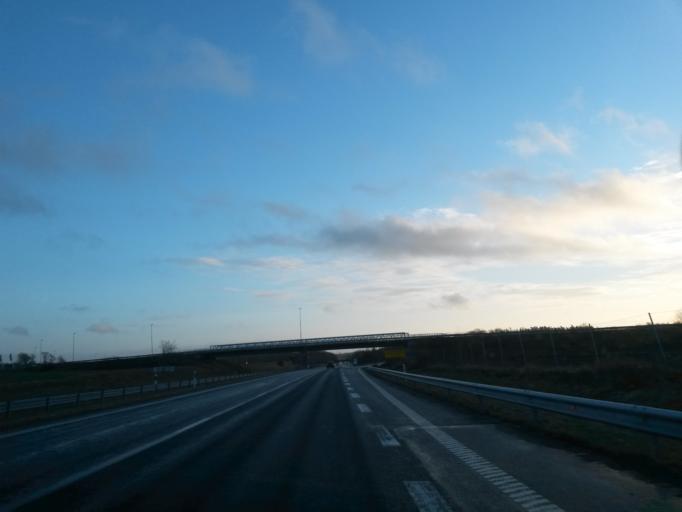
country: SE
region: Halland
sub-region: Halmstads Kommun
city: Halmstad
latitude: 56.7160
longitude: 12.8868
